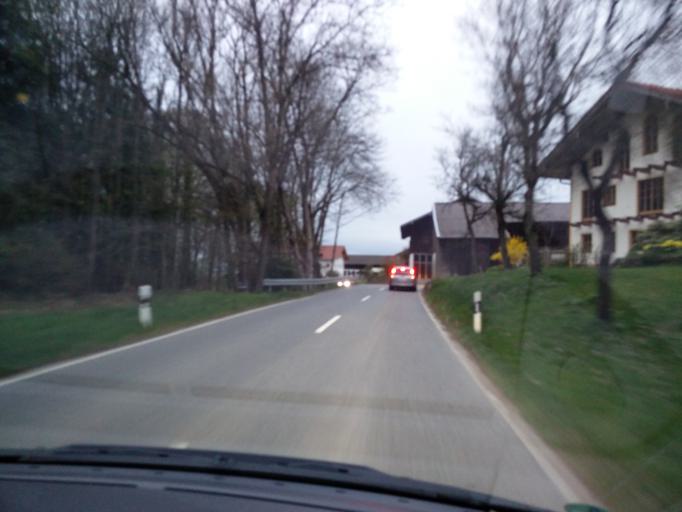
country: DE
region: Bavaria
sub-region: Upper Bavaria
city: Amerang
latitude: 47.9762
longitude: 12.2973
